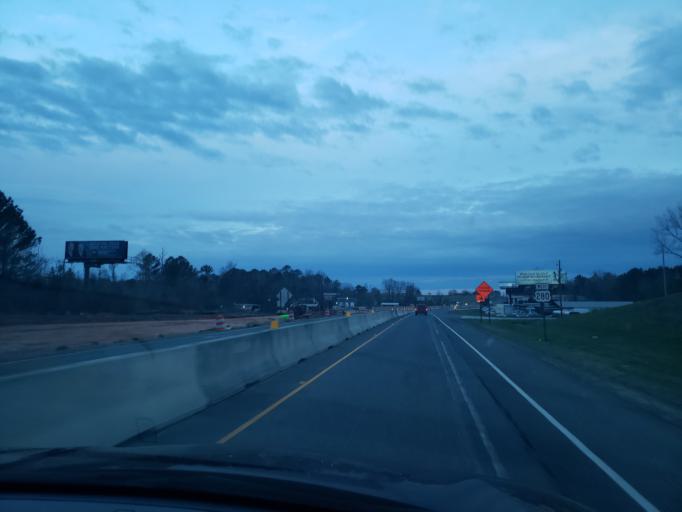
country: US
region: Alabama
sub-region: Lee County
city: Auburn
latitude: 32.6772
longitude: -85.4869
